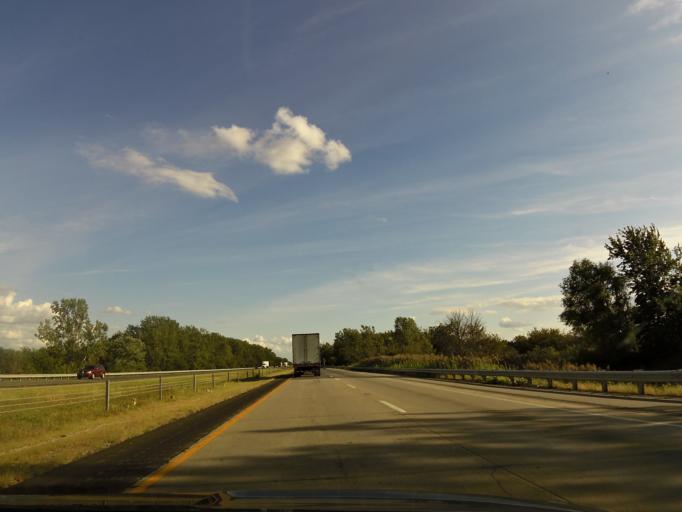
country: US
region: Indiana
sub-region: Jasper County
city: Rensselaer
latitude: 40.9111
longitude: -87.2127
